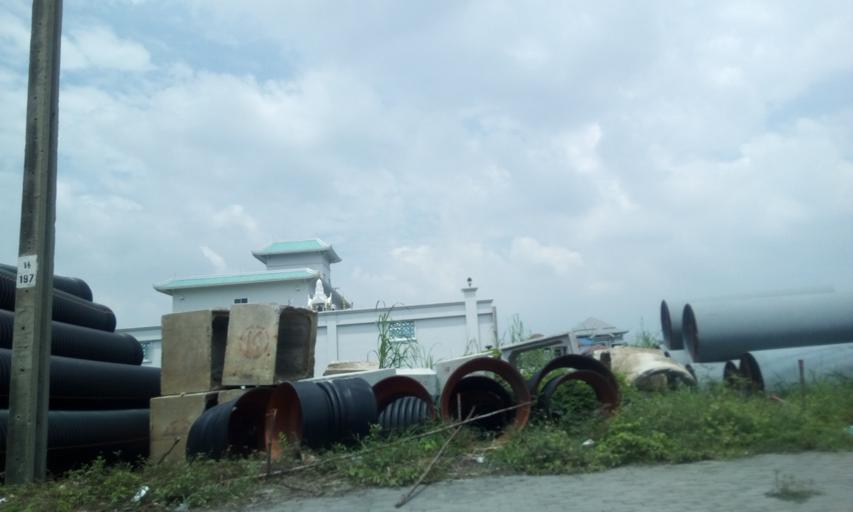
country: TH
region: Bangkok
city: Don Mueang
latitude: 13.9376
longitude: 100.5562
